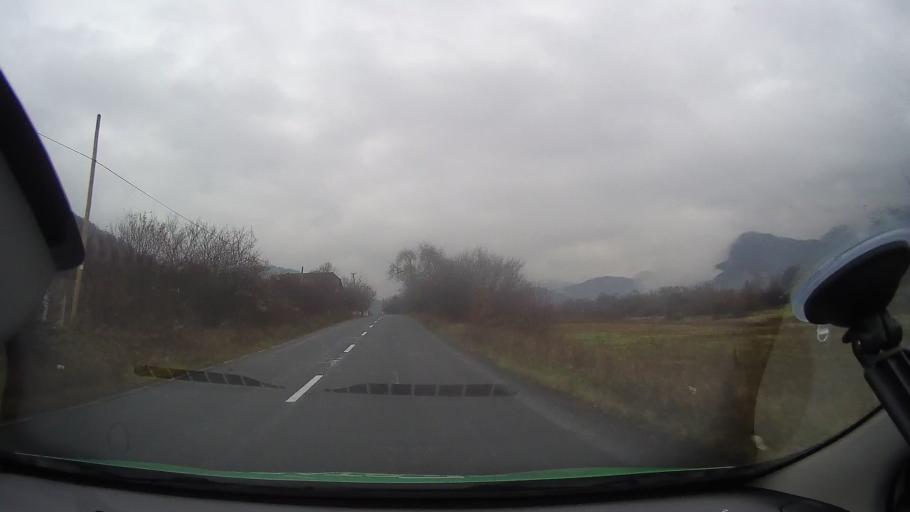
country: RO
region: Arad
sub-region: Comuna Plescuta
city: Plescuta
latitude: 46.2966
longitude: 22.4308
